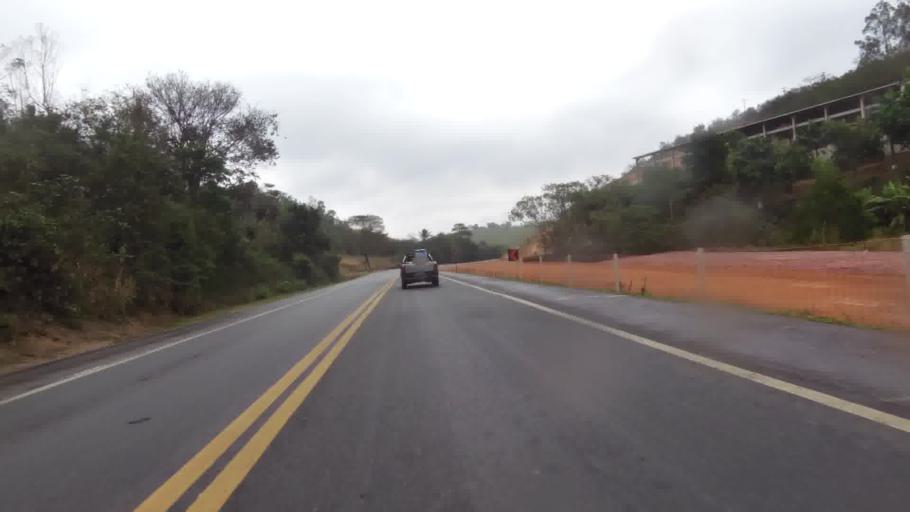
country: BR
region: Espirito Santo
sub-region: Rio Novo Do Sul
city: Rio Novo do Sul
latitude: -20.8975
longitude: -41.0100
